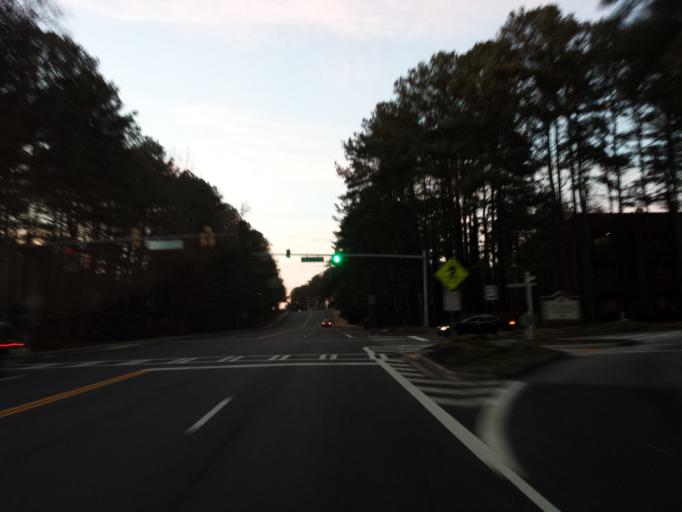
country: US
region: Georgia
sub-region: Cobb County
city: Smyrna
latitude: 33.8948
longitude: -84.4917
